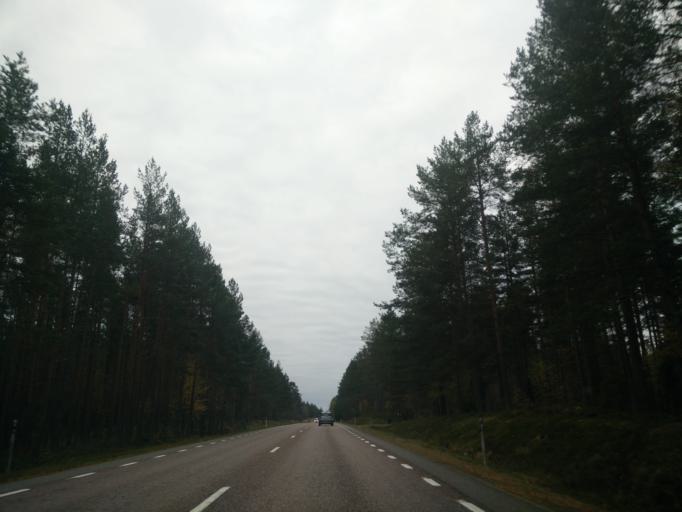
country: SE
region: Gaevleborg
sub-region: Gavle Kommun
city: Norrsundet
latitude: 60.8316
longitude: 17.2084
